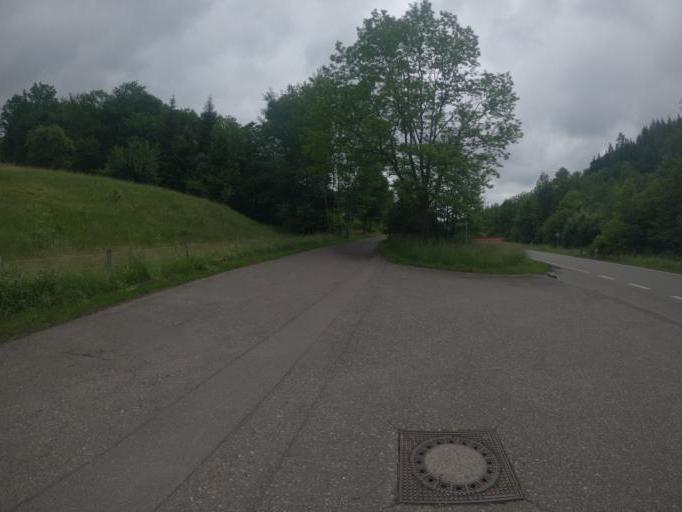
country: DE
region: Baden-Wuerttemberg
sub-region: Regierungsbezirk Stuttgart
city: Ebersbach an der Fils
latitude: 48.7476
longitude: 9.5398
